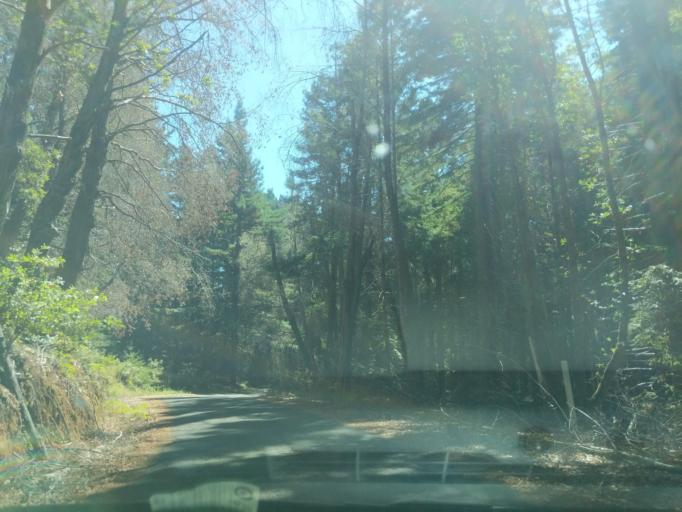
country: US
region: California
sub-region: Sonoma County
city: Monte Rio
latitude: 38.5247
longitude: -123.2315
